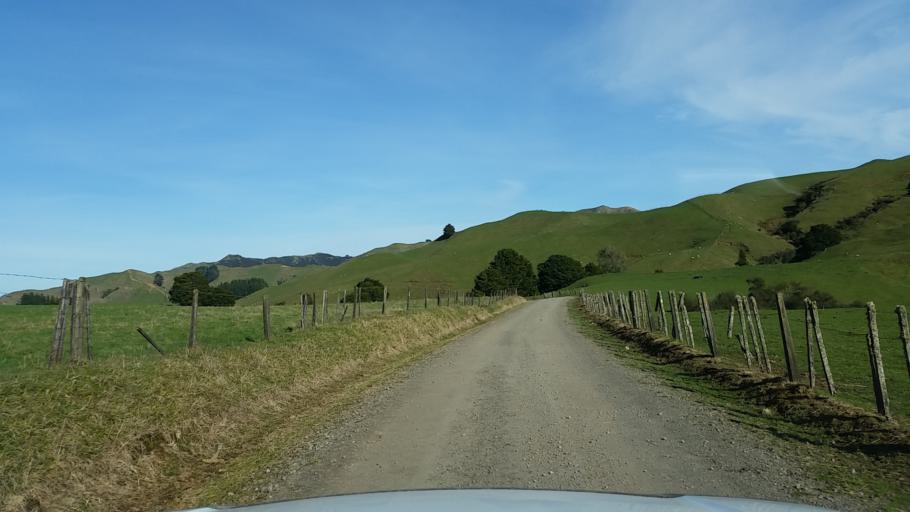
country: NZ
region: Taranaki
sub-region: South Taranaki District
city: Eltham
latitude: -39.3124
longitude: 174.5371
